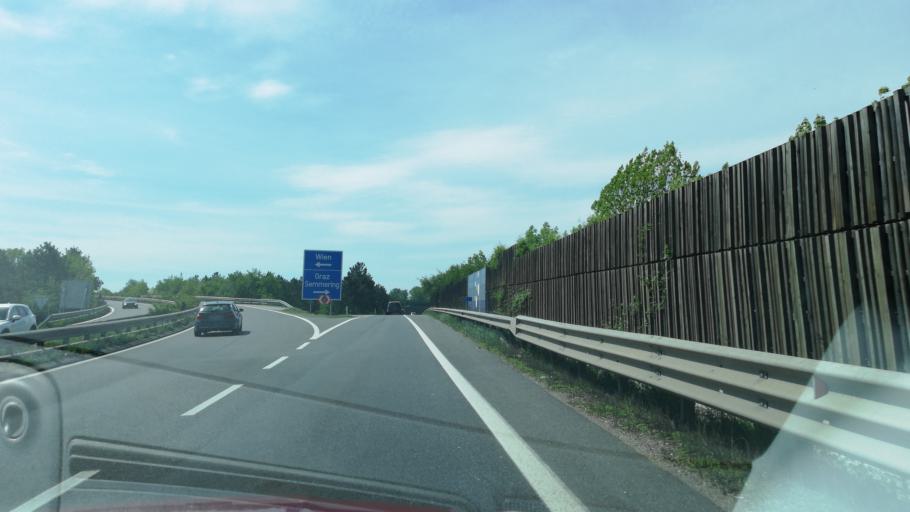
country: AT
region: Lower Austria
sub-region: Politischer Bezirk Baden
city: Traiskirchen
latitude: 47.9888
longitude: 16.2776
